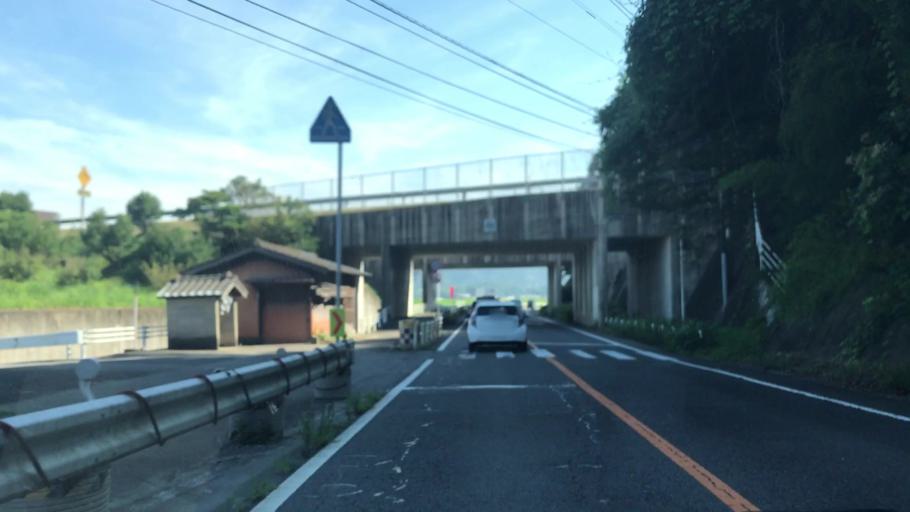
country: JP
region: Saga Prefecture
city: Takeocho-takeo
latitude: 33.2065
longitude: 130.0576
